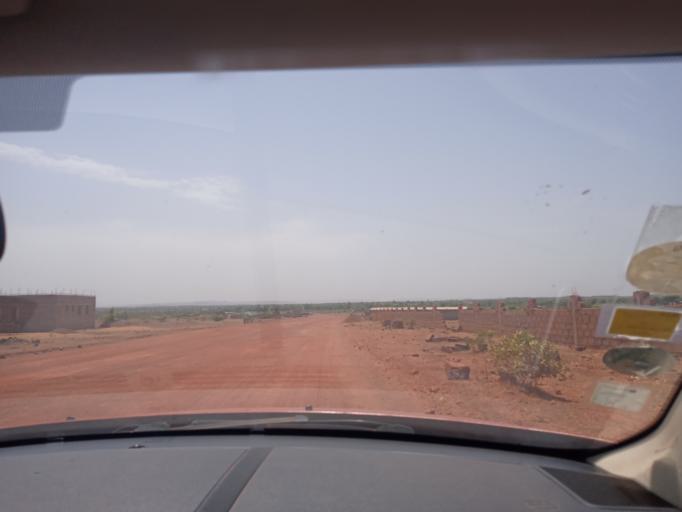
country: ML
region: Bamako
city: Bamako
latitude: 12.5173
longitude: -7.7914
